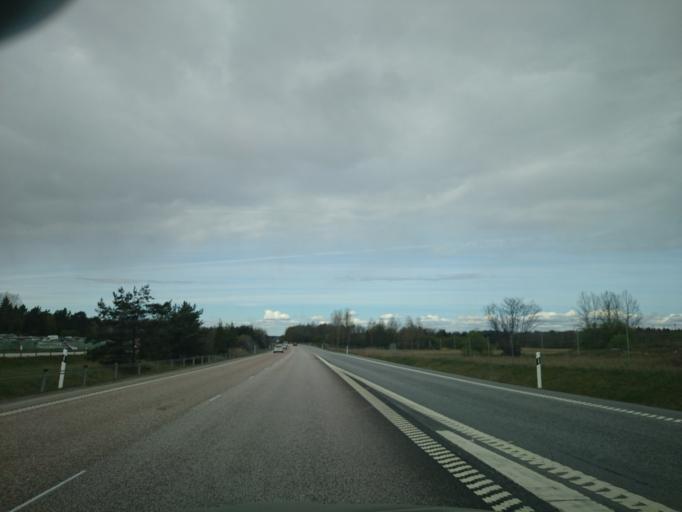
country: SE
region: Stockholm
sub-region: Sigtuna Kommun
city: Marsta
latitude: 59.6335
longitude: 17.8992
